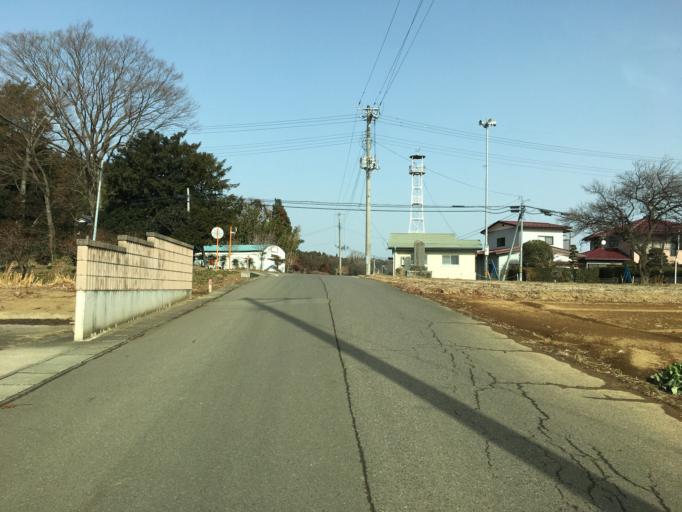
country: JP
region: Fukushima
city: Nihommatsu
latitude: 37.5623
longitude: 140.3988
